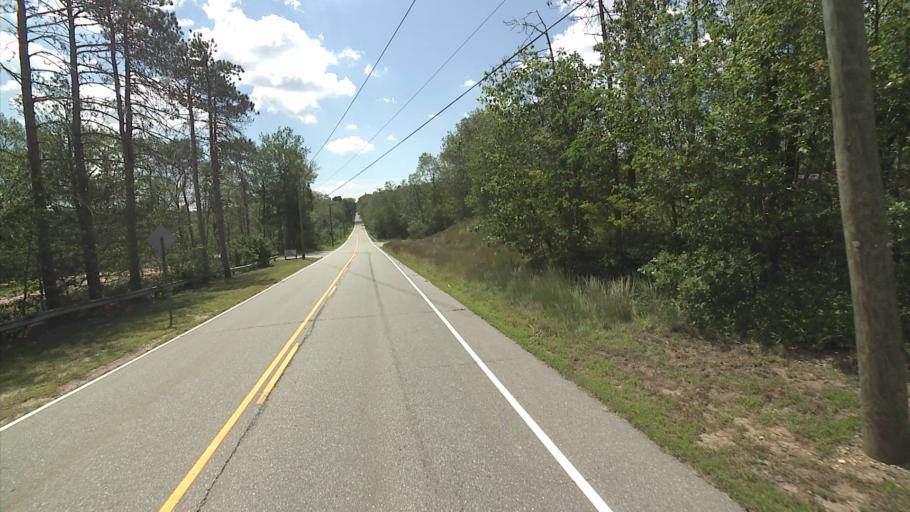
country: US
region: Connecticut
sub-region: Windham County
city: Windham
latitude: 41.7995
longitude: -72.1253
